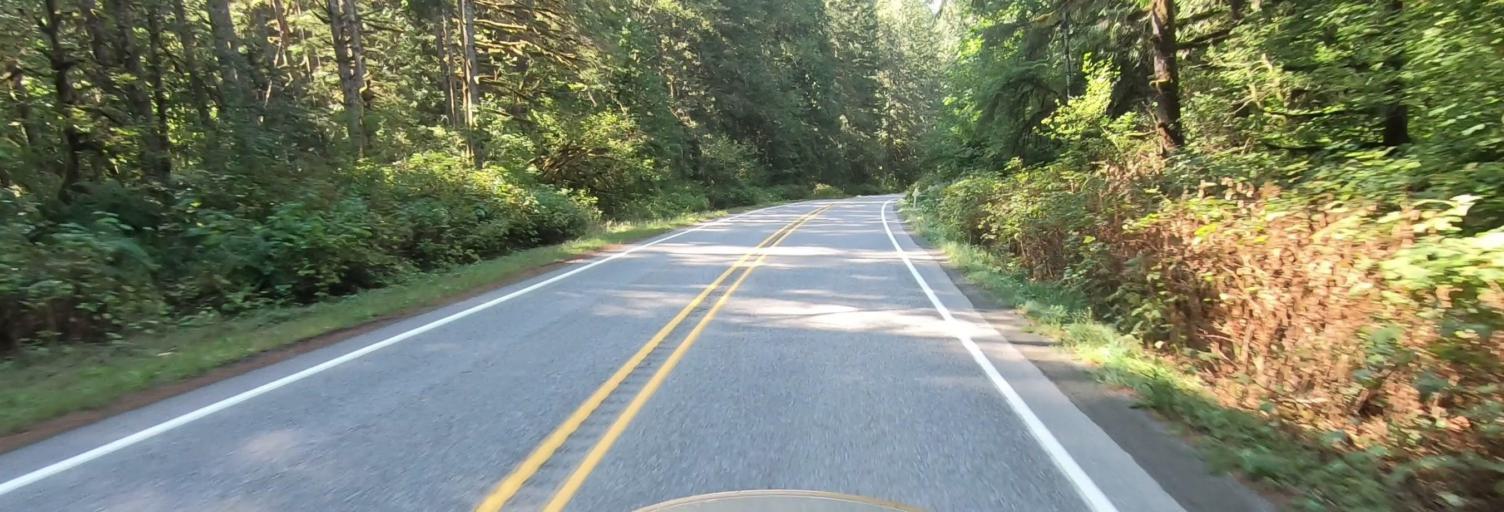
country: US
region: Washington
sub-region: Whatcom County
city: Peaceful Valley
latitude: 48.8980
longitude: -121.9350
